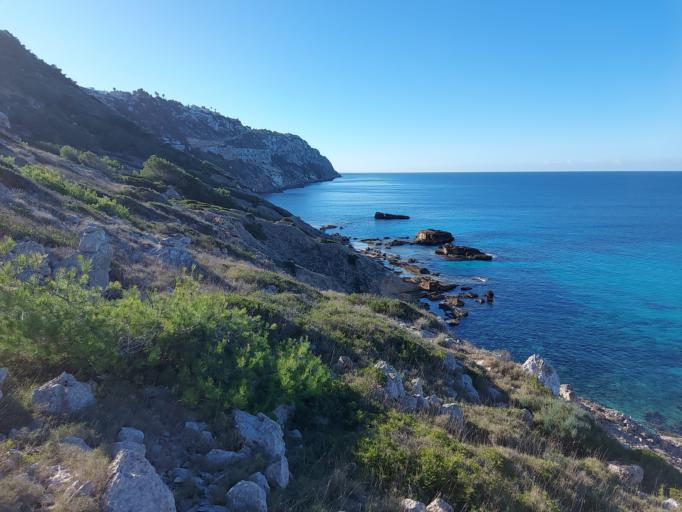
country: ES
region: Balearic Islands
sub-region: Illes Balears
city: s'Arenal
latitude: 39.4419
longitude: 2.7476
